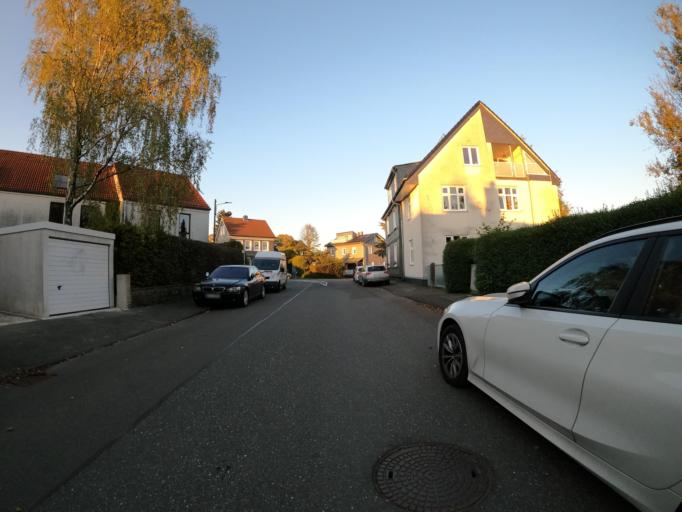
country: DE
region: North Rhine-Westphalia
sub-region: Regierungsbezirk Dusseldorf
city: Wuppertal
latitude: 51.2280
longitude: 7.1324
